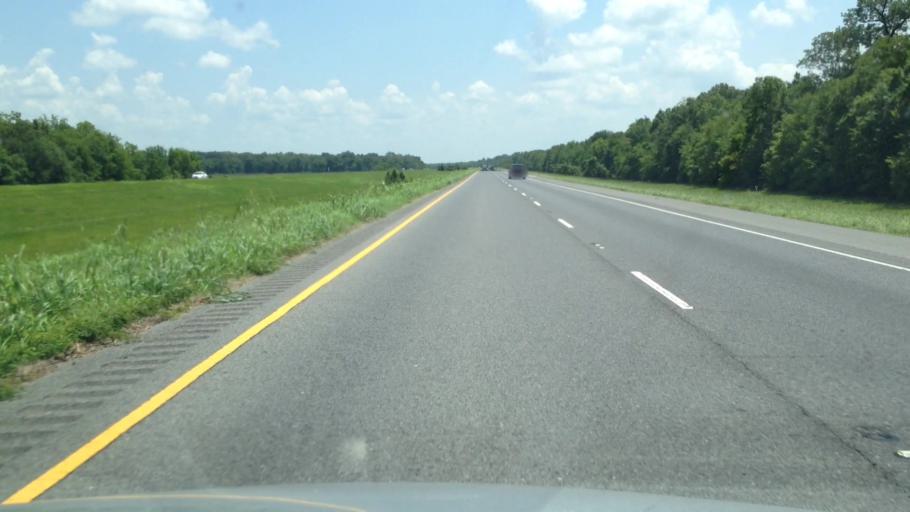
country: US
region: Louisiana
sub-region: Avoyelles Parish
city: Bunkie
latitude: 30.8276
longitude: -92.2257
